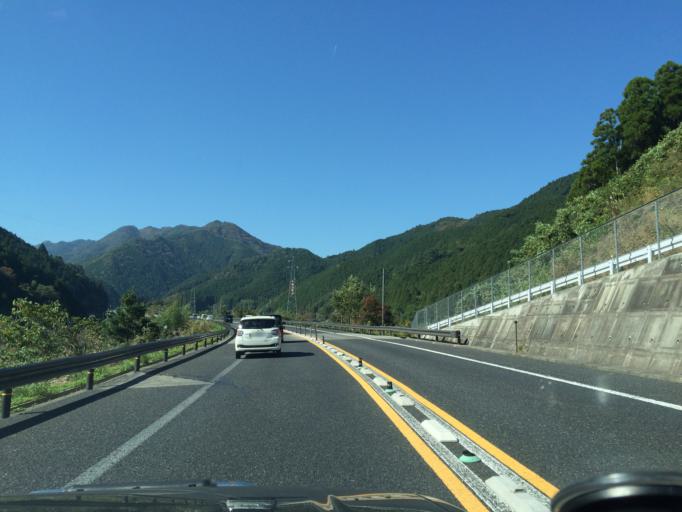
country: JP
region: Kyoto
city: Fukuchiyama
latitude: 35.2909
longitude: 134.9728
